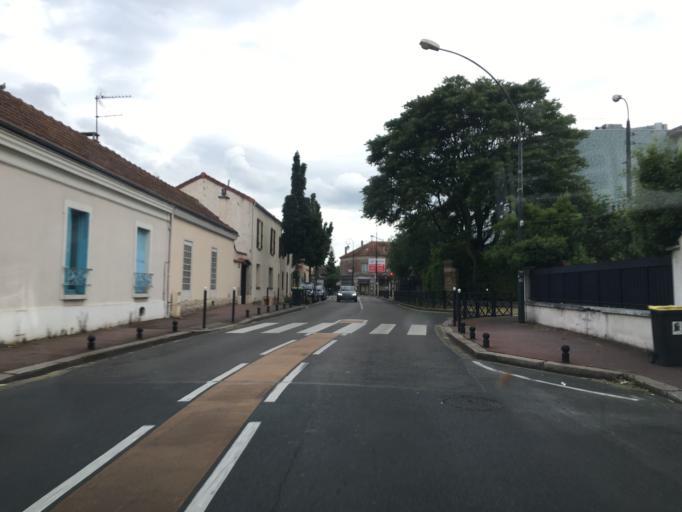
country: FR
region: Ile-de-France
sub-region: Departement du Val-de-Marne
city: Saint-Maur-des-Fosses
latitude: 48.7899
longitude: 2.4958
